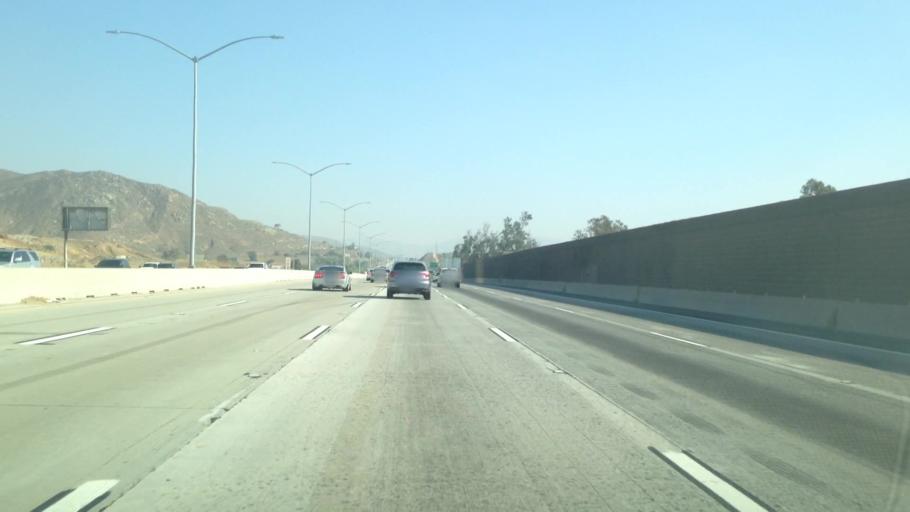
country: US
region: California
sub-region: Riverside County
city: Glen Avon
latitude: 34.0178
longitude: -117.4723
